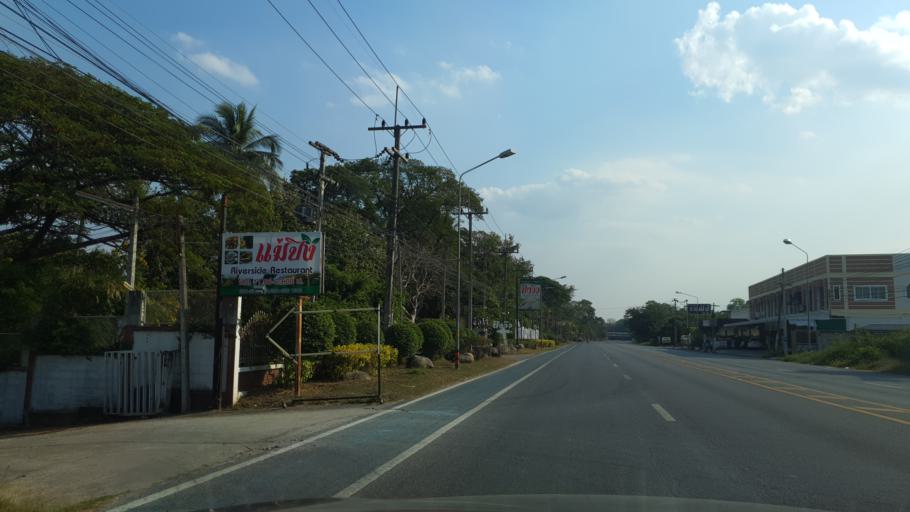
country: TH
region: Tak
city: Tak
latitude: 16.8620
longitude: 99.1210
